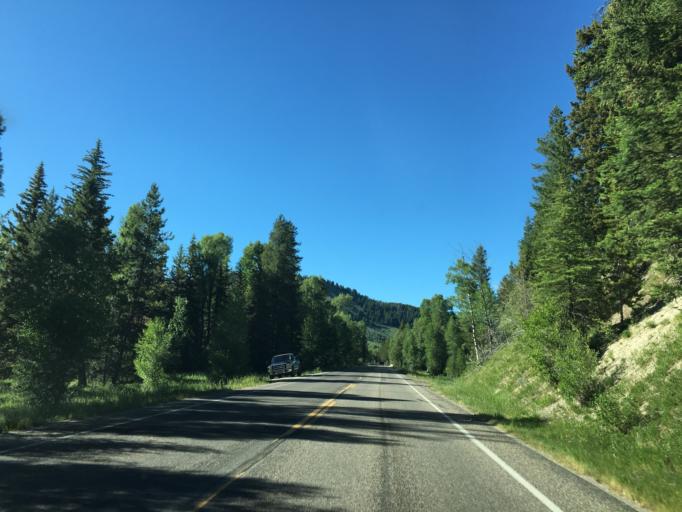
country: US
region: Wyoming
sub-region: Teton County
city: Jackson
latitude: 43.8484
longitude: -110.5176
